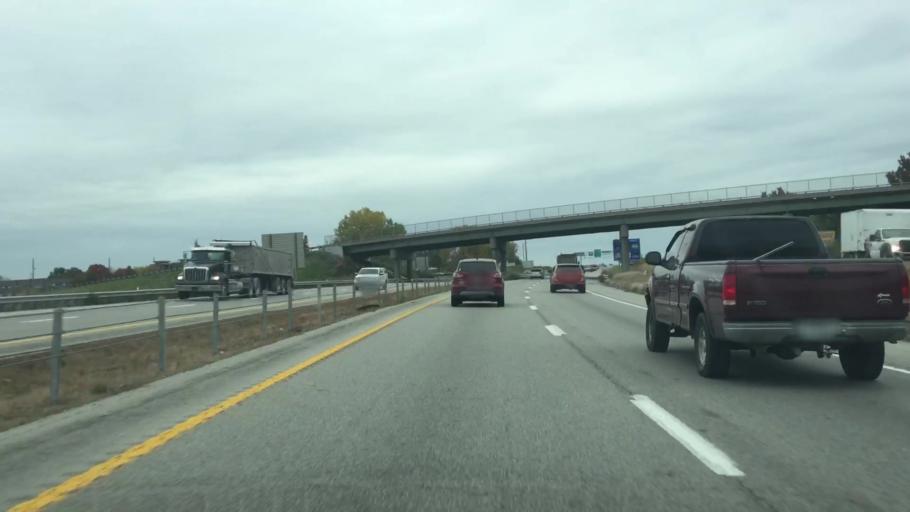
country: US
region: Missouri
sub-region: Jackson County
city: Lees Summit
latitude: 38.9179
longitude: -94.4009
